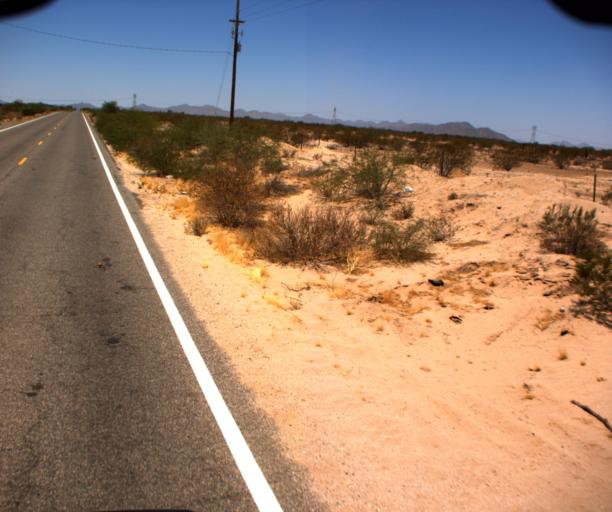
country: US
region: Arizona
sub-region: Pinal County
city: Maricopa
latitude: 33.0545
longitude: -112.2757
